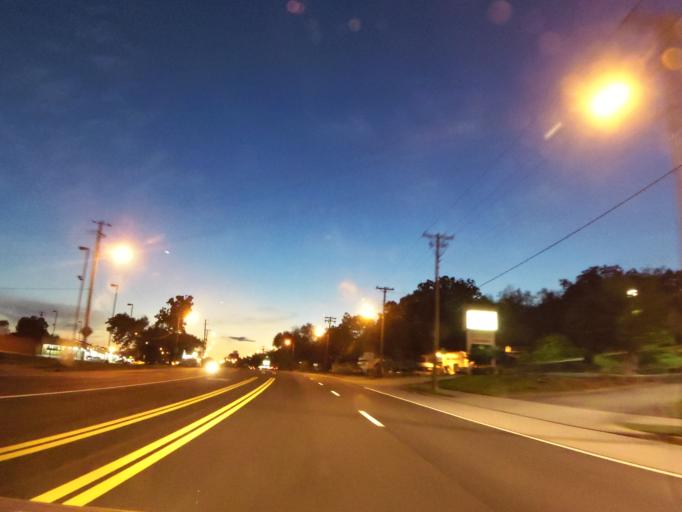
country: US
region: Tennessee
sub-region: Knox County
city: Knoxville
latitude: 36.0046
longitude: -83.8658
